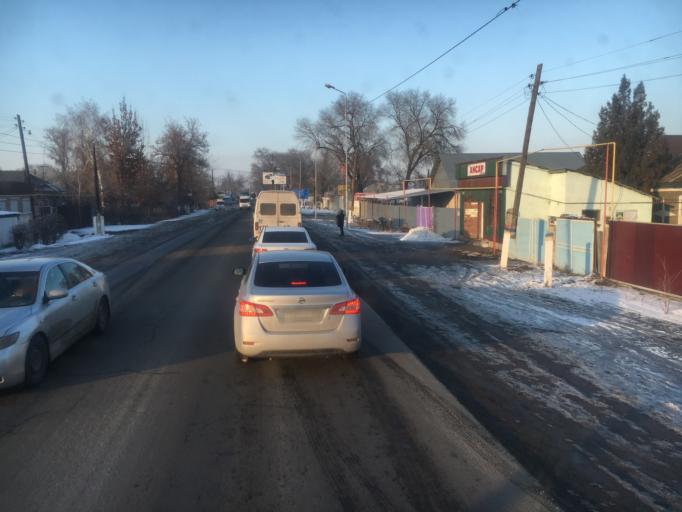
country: KZ
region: Almaty Oblysy
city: Burunday
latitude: 43.3737
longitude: 76.6418
